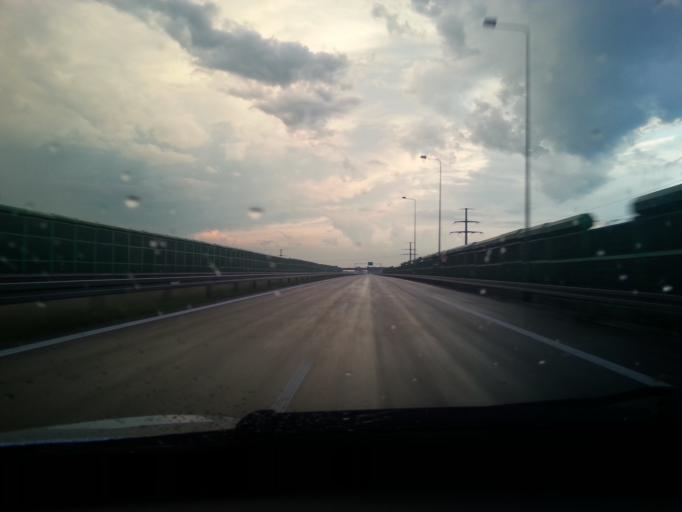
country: PL
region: Lodz Voivodeship
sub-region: Powiat pabianicki
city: Pabianice
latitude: 51.6813
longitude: 19.3259
